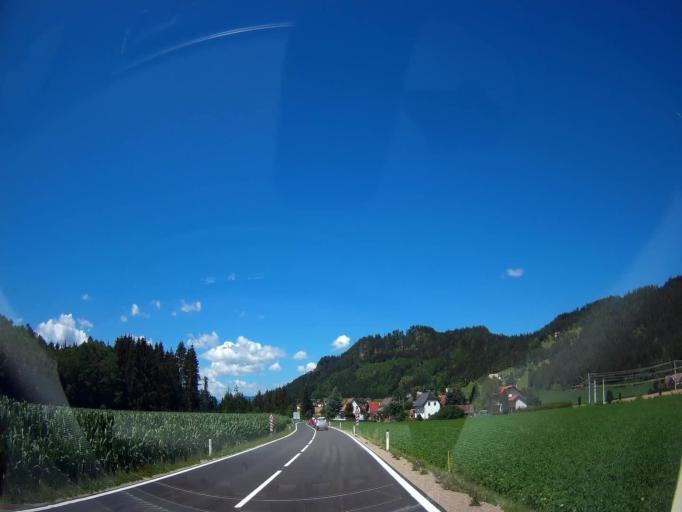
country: AT
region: Carinthia
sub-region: Politischer Bezirk Sankt Veit an der Glan
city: St. Georgen am Laengsee
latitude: 46.7646
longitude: 14.4496
